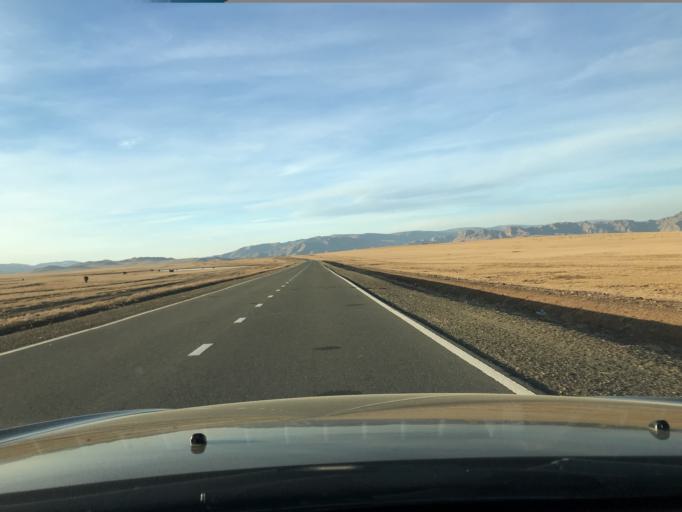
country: MN
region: Central Aimak
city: Arhust
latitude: 47.7526
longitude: 107.4499
